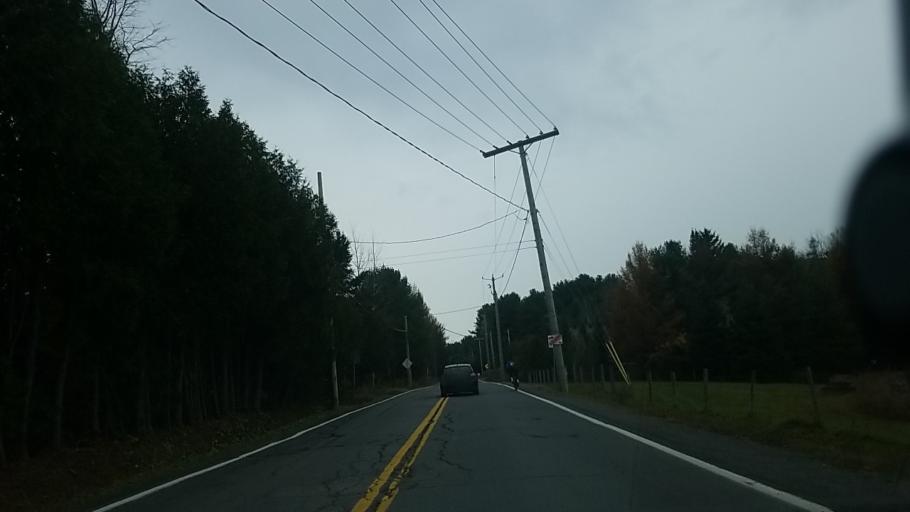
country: CA
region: Quebec
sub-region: Laurentides
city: Saint-Colomban
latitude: 45.7846
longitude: -74.0923
